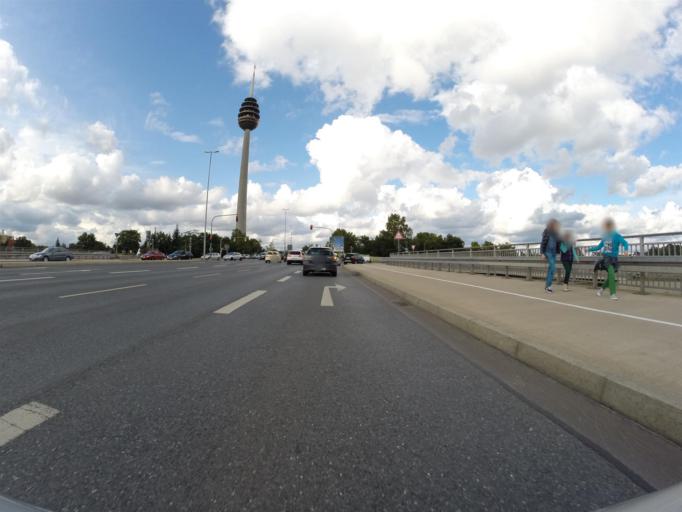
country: DE
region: Bavaria
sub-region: Regierungsbezirk Mittelfranken
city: Grossreuth bei Schweinau
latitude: 49.4224
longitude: 11.0374
